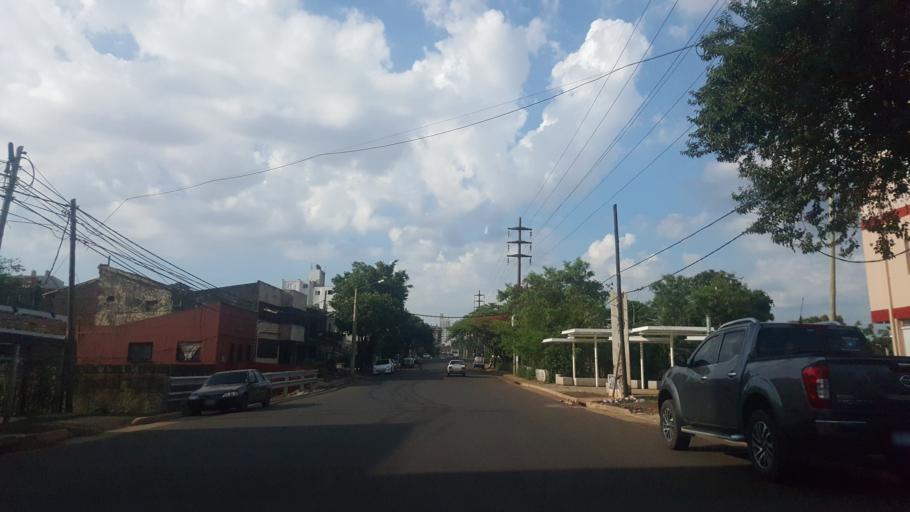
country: AR
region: Misiones
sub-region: Departamento de Capital
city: Posadas
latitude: -27.3809
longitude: -55.8918
